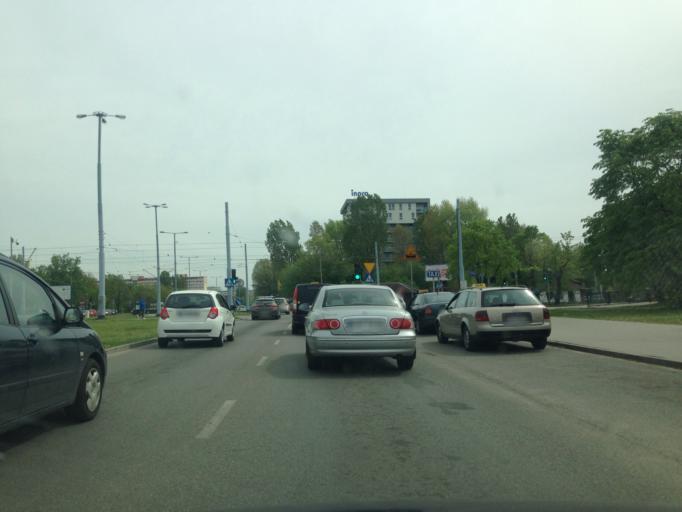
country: PL
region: Pomeranian Voivodeship
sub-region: Sopot
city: Sopot
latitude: 54.4205
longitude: 18.5828
